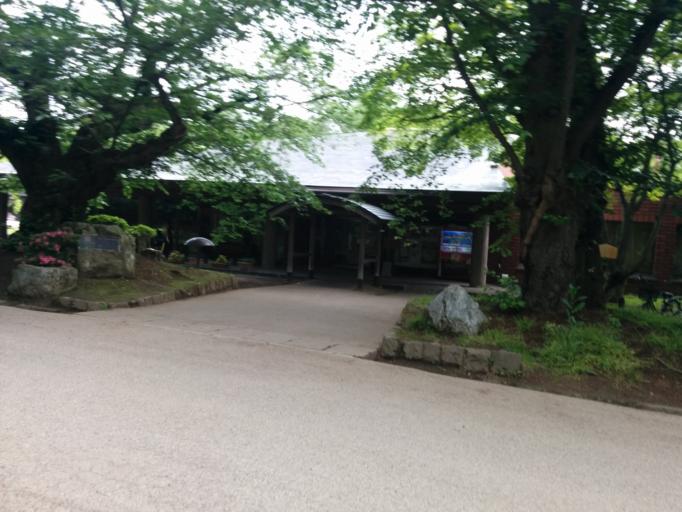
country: JP
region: Aomori
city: Hirosaki
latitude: 40.6092
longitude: 140.4676
